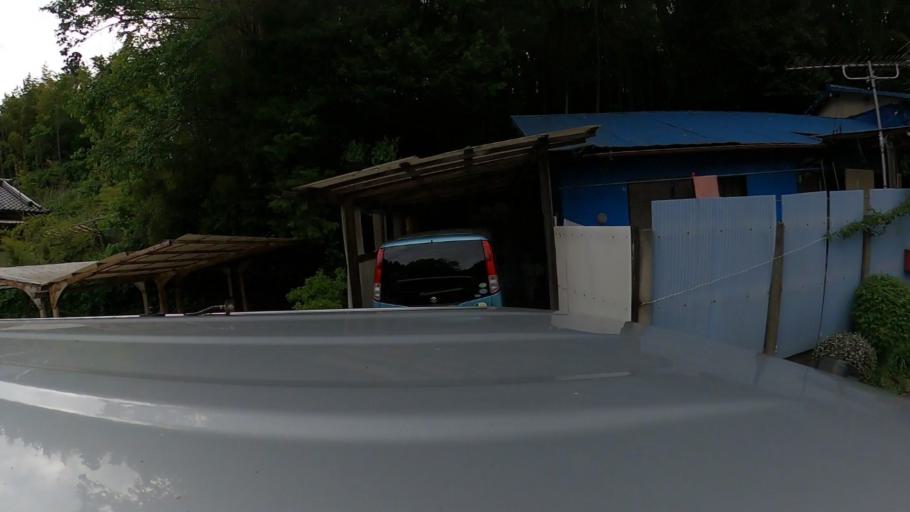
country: JP
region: Ibaraki
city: Ami
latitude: 35.9714
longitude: 140.2314
